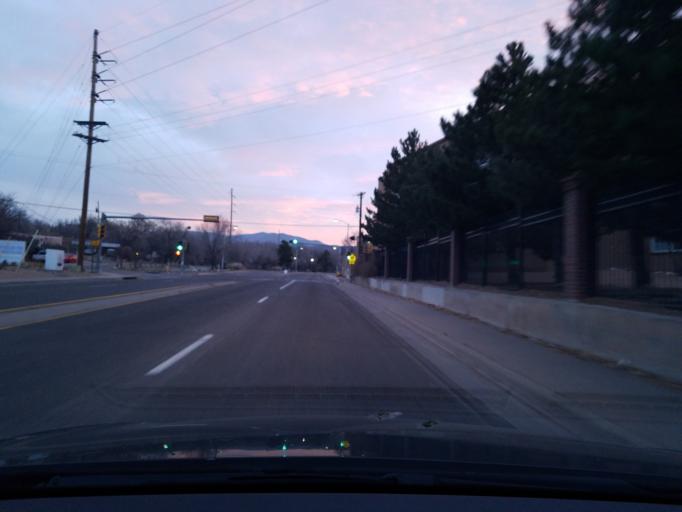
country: US
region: New Mexico
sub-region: Santa Fe County
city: Santa Fe
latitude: 35.6919
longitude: -105.9434
